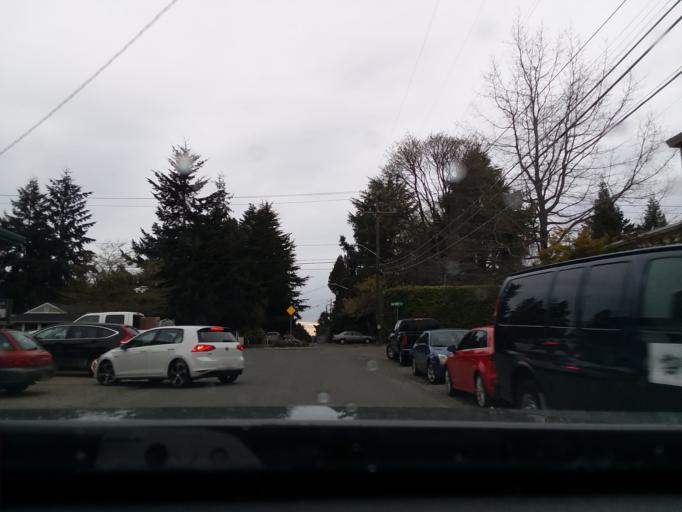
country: US
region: Washington
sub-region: King County
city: Shoreline
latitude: 47.6976
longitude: -122.3741
